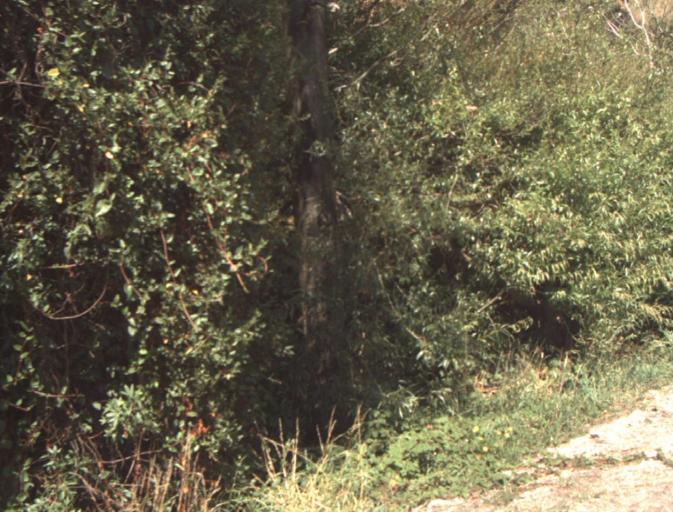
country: AU
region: Tasmania
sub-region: Launceston
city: Mayfield
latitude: -41.2601
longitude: 147.1760
